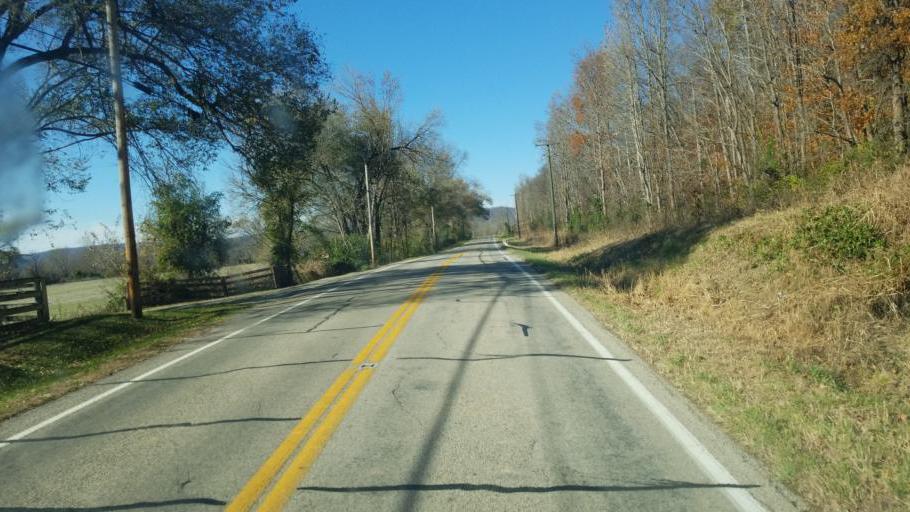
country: US
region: Kentucky
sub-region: Lewis County
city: Vanceburg
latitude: 38.6242
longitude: -83.1952
